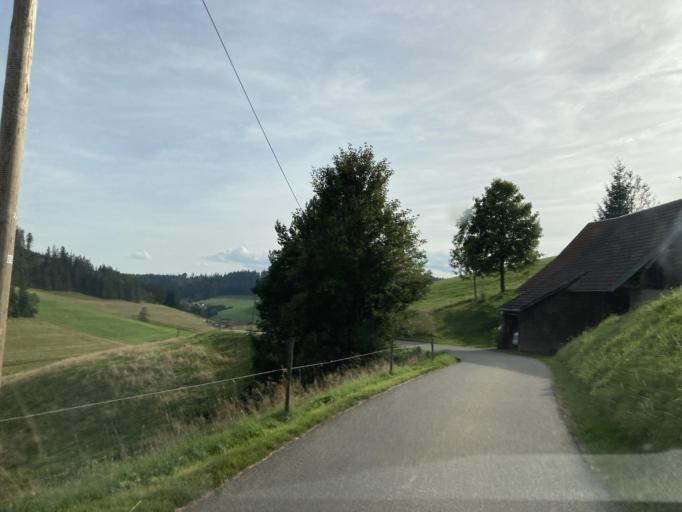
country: DE
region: Baden-Wuerttemberg
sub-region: Freiburg Region
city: Titisee-Neustadt
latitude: 47.9876
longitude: 8.1787
